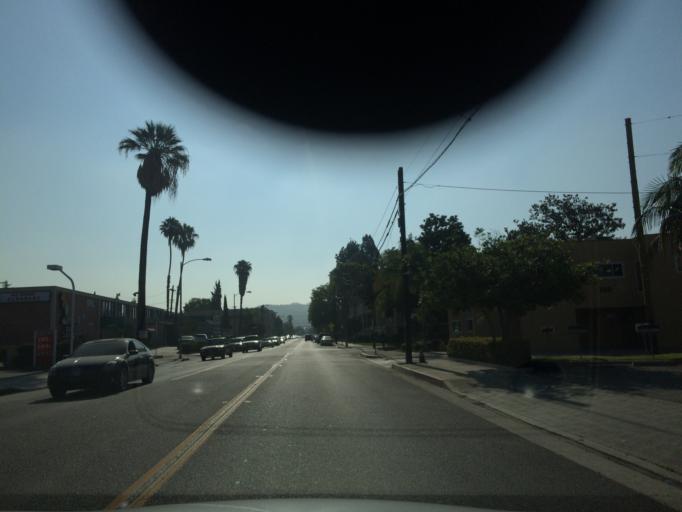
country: US
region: California
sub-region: Los Angeles County
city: Glendale
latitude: 34.1482
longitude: -118.2461
